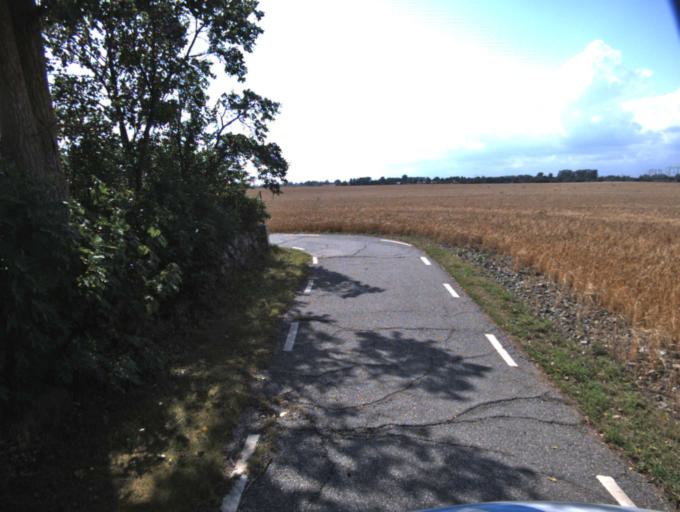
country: SE
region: Skane
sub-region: Kavlinge Kommun
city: Kaevlinge
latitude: 55.8141
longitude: 13.1084
